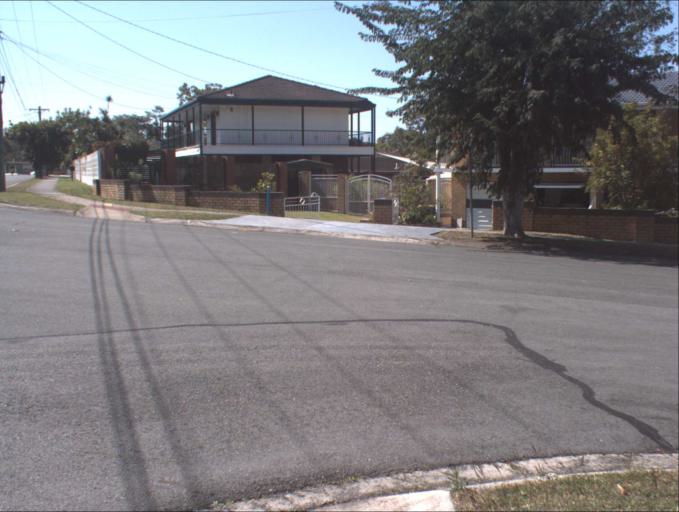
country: AU
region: Queensland
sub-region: Logan
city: Rochedale South
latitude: -27.5963
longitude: 153.1138
